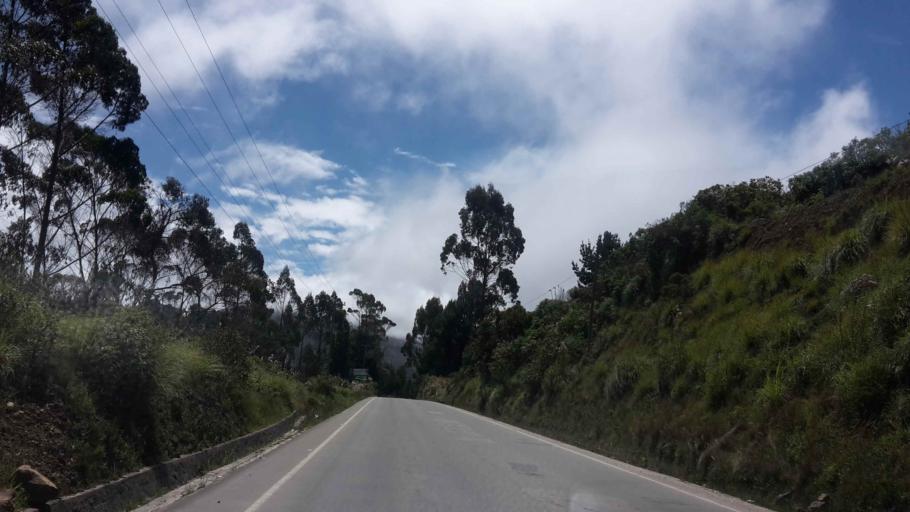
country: BO
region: Cochabamba
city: Colomi
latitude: -17.2670
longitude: -65.8824
